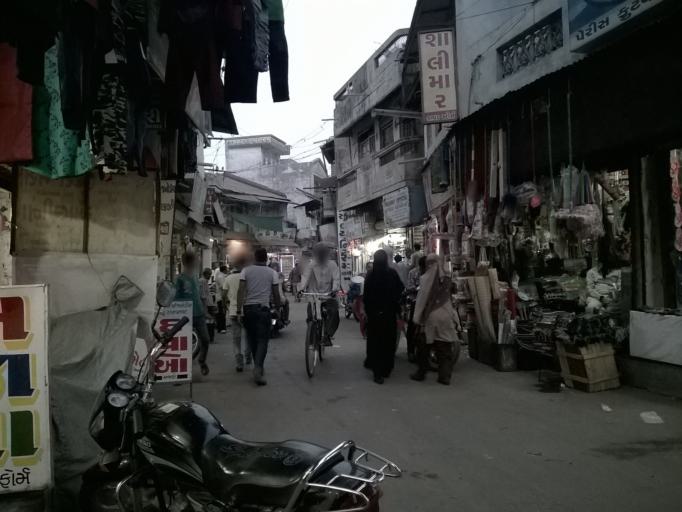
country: IN
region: Gujarat
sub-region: Kheda
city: Nadiad
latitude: 22.6970
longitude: 72.8623
